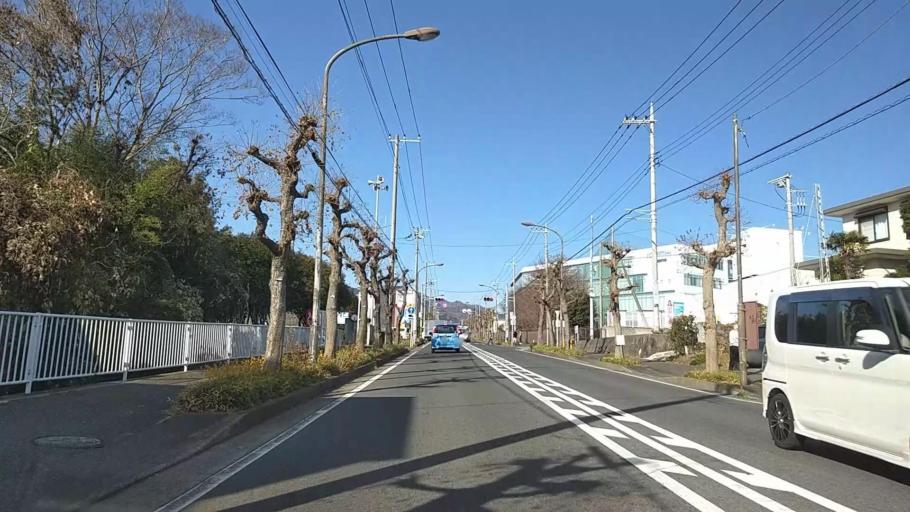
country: JP
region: Kanagawa
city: Isehara
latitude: 35.4014
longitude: 139.2972
